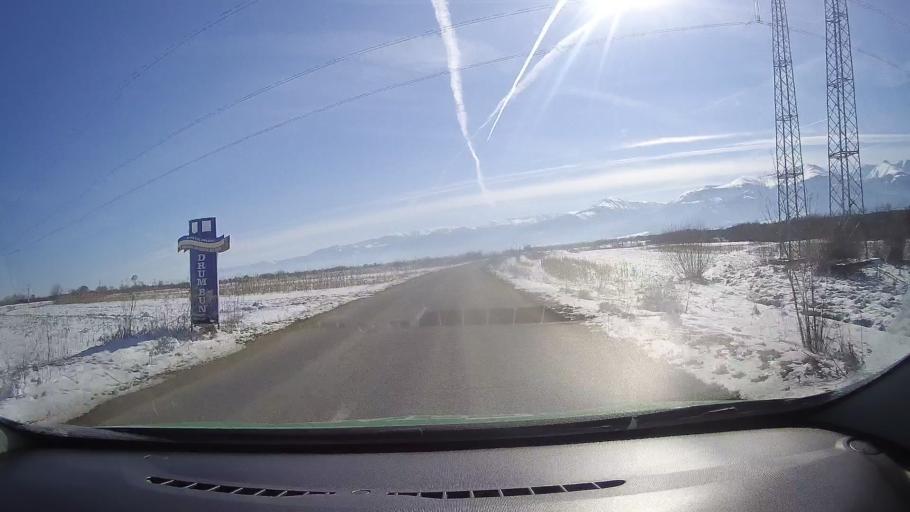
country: RO
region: Brasov
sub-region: Comuna Sambata de Sus
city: Sambata de Sus
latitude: 45.7542
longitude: 24.8338
